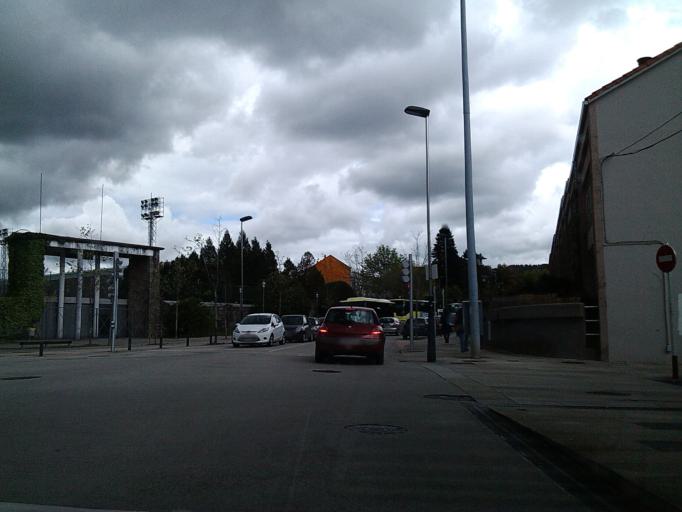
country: ES
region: Galicia
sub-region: Provincia da Coruna
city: Santiago de Compostela
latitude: 42.8844
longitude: -8.5481
